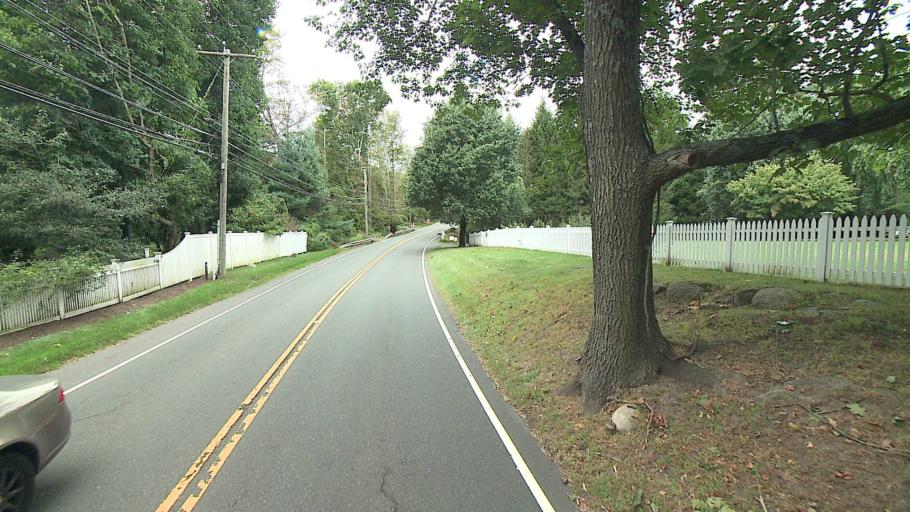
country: US
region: Connecticut
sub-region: Fairfield County
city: Wilton
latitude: 41.2009
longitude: -73.4458
